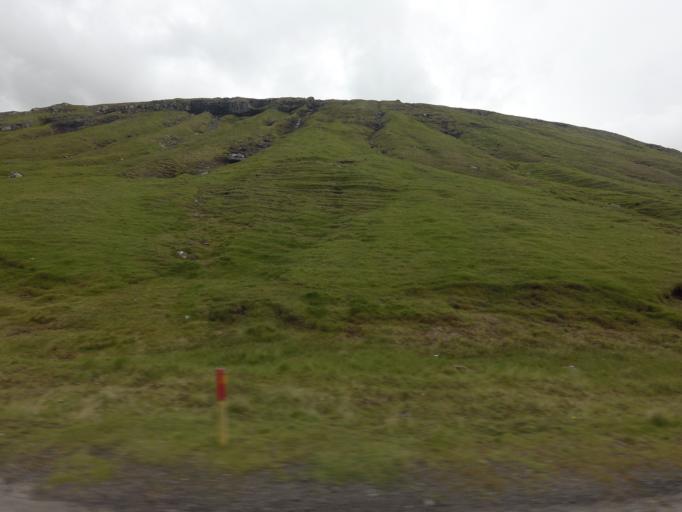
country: FO
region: Streymoy
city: Kollafjordhur
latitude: 62.1270
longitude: -7.0033
